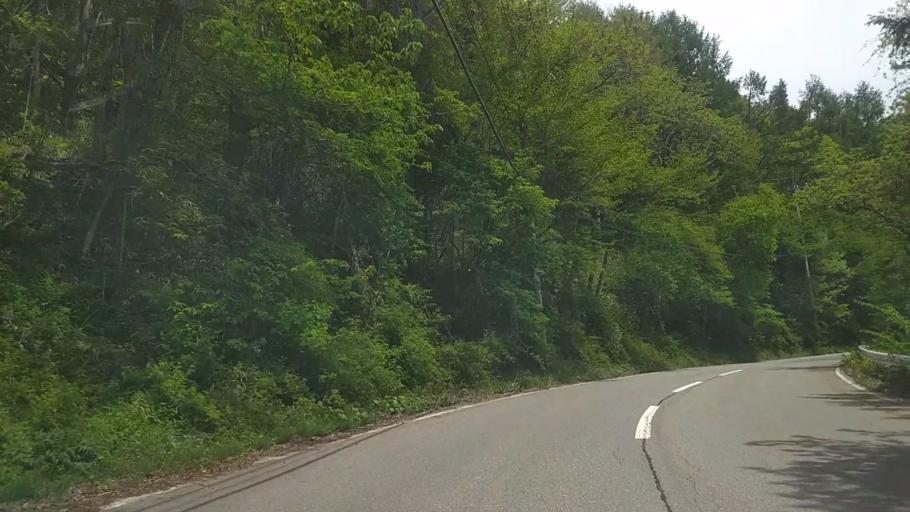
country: JP
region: Nagano
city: Saku
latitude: 36.1058
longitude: 138.4110
